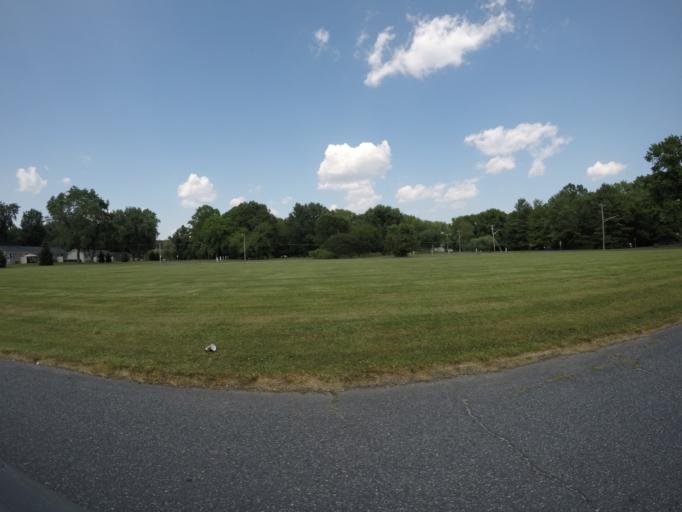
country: US
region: Maryland
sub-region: Harford County
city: Edgewood
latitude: 39.4151
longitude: -76.2994
